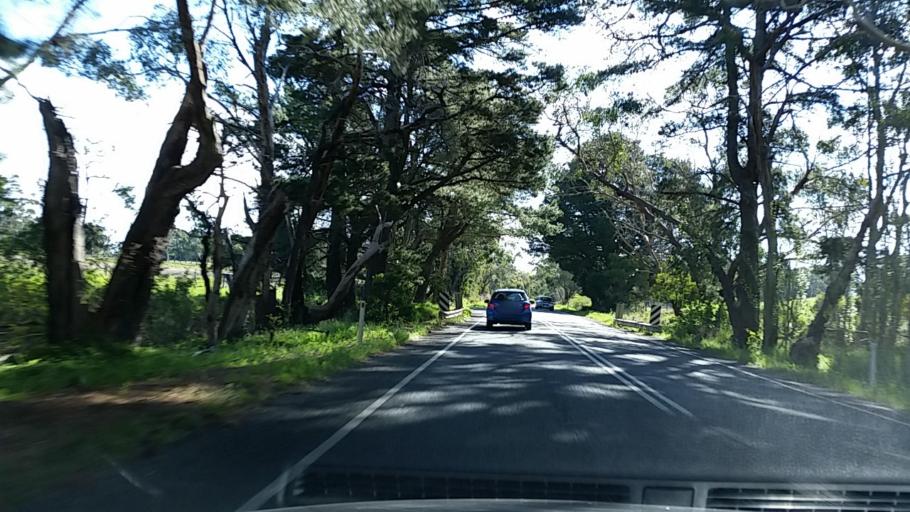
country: AU
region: South Australia
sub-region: Alexandrina
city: Mount Compass
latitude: -35.2921
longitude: 138.6007
